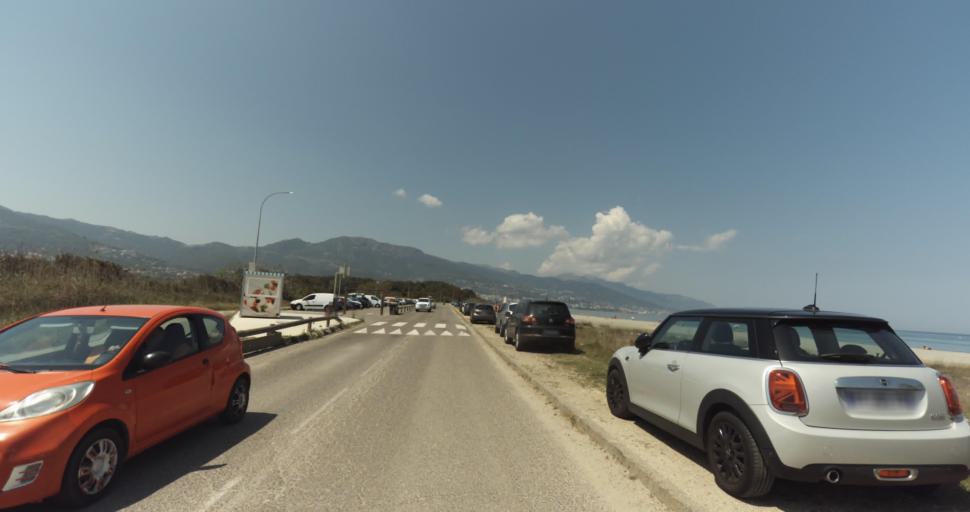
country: FR
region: Corsica
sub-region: Departement de la Haute-Corse
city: Biguglia
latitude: 42.6409
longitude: 9.4609
